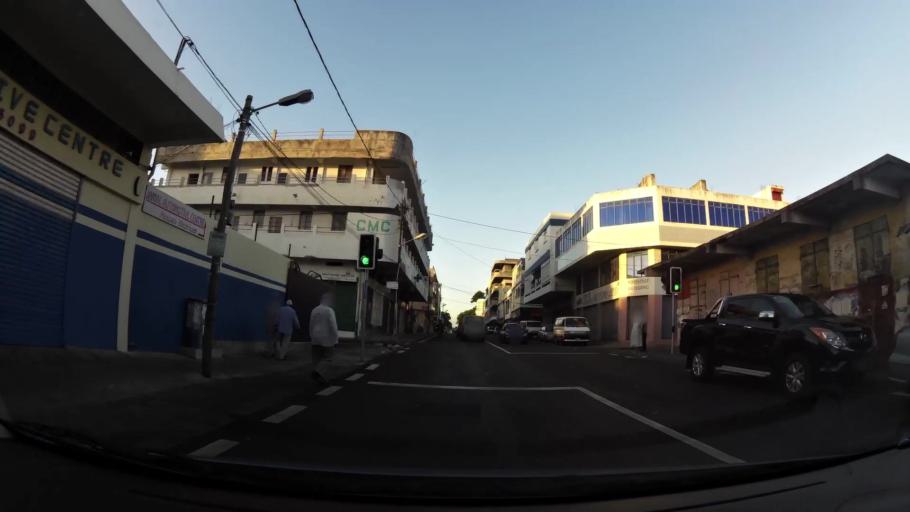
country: MU
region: Port Louis
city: Port Louis
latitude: -20.1554
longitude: 57.5099
